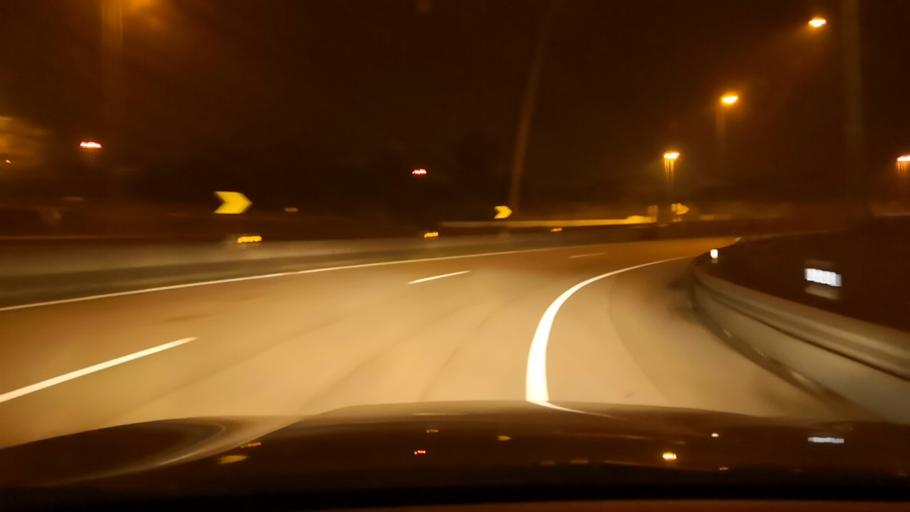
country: PT
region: Porto
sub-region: Maia
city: Leca do Bailio
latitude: 41.2020
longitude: -8.6287
